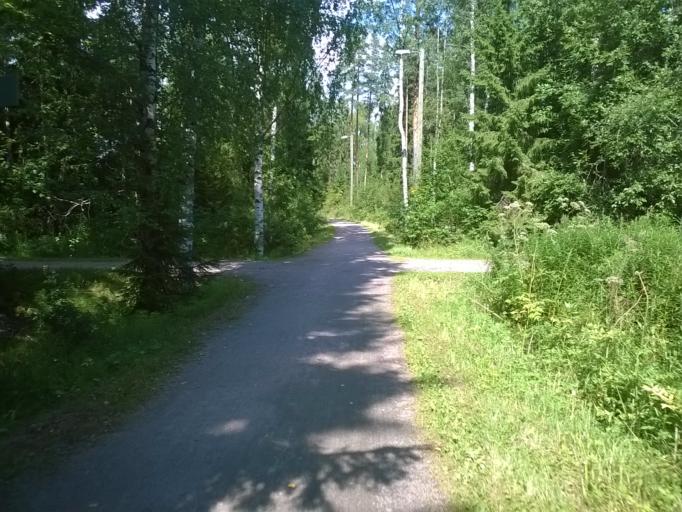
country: FI
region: Uusimaa
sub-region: Helsinki
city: Teekkarikylae
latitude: 60.2655
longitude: 24.9019
